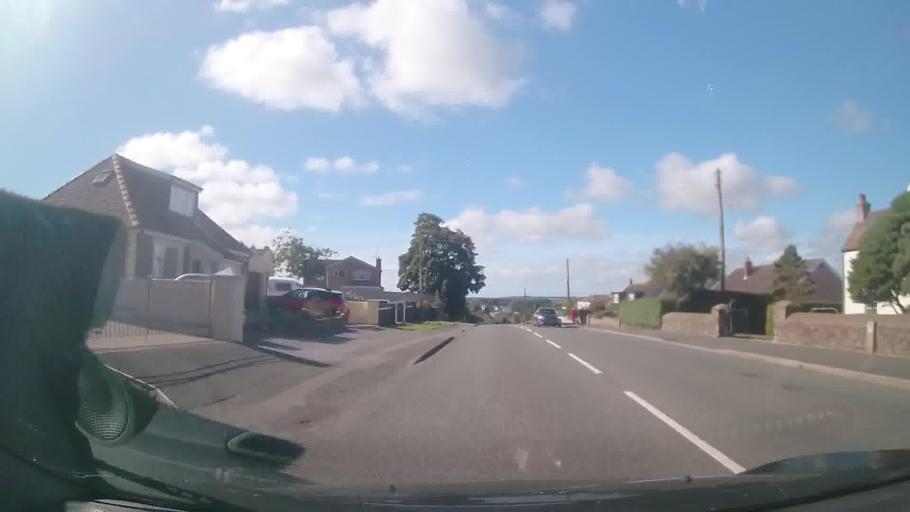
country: GB
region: Wales
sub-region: Pembrokeshire
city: Kilgetty
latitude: 51.7209
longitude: -4.7281
